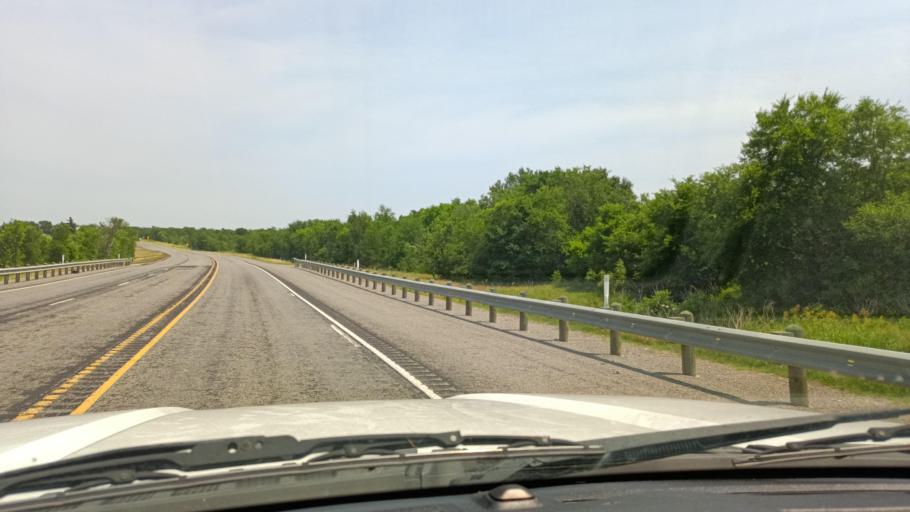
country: US
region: Texas
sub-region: Bell County
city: Rogers
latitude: 30.8794
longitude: -97.1449
